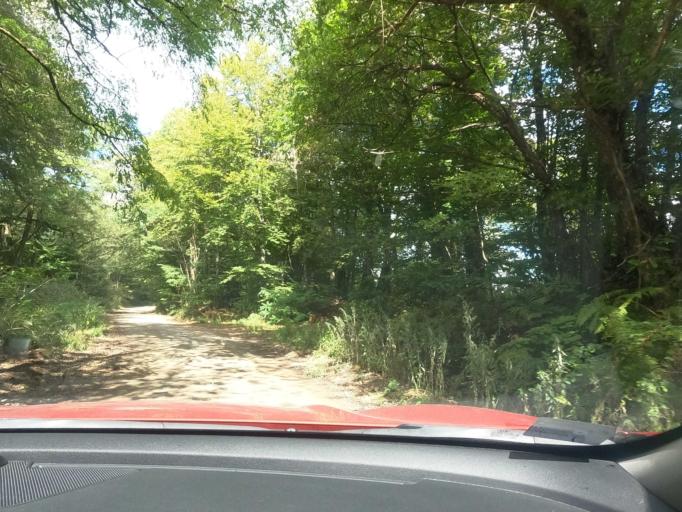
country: HR
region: Sisacko-Moslavacka
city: Gvozd
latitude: 45.3304
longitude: 15.8420
